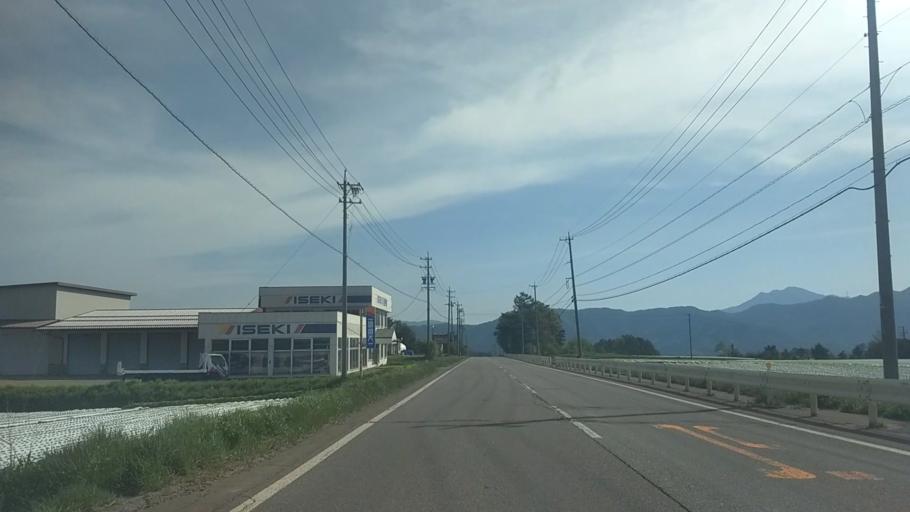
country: JP
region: Nagano
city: Saku
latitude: 35.9897
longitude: 138.4891
